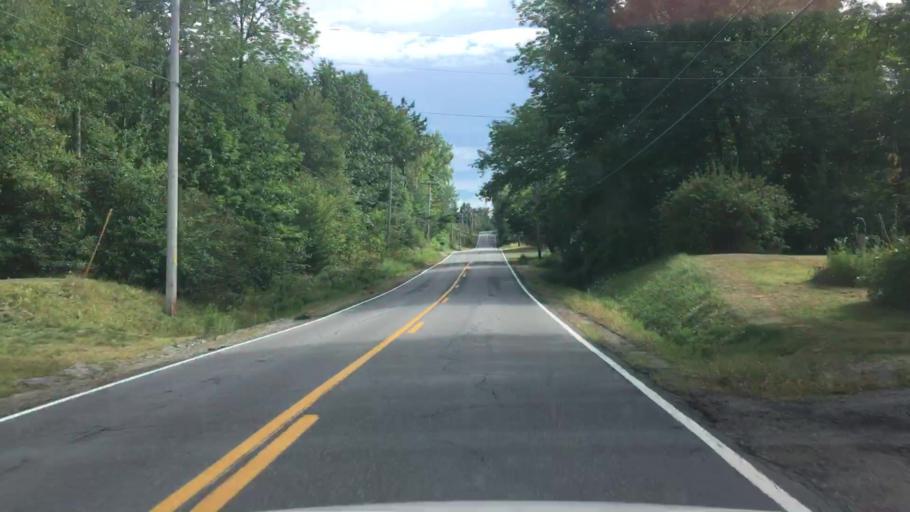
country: US
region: Maine
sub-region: Hancock County
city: Ellsworth
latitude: 44.4931
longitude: -68.4202
